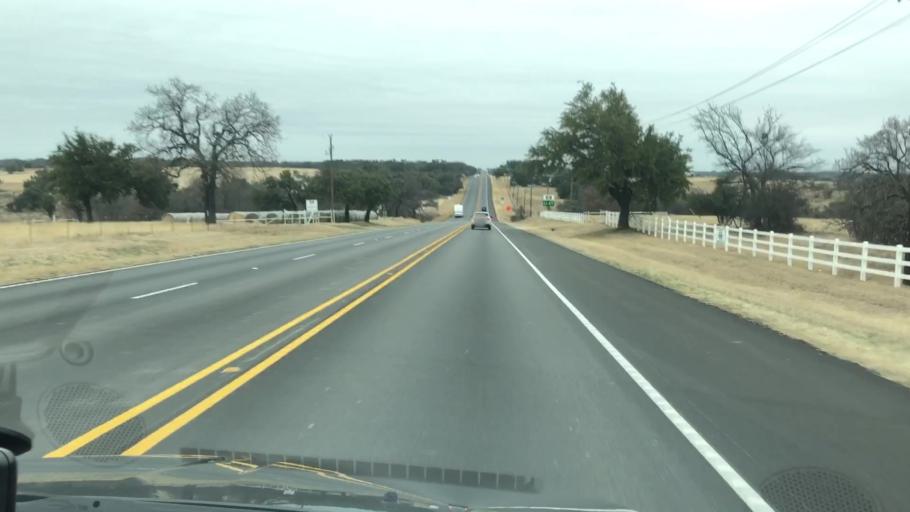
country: US
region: Texas
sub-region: Erath County
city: Stephenville
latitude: 32.2999
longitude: -98.1879
